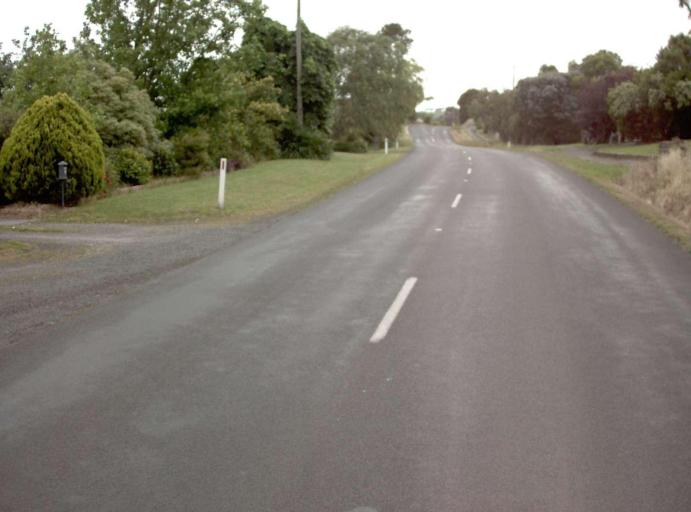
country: AU
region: Victoria
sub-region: Bass Coast
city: North Wonthaggi
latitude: -38.4411
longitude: 145.8102
